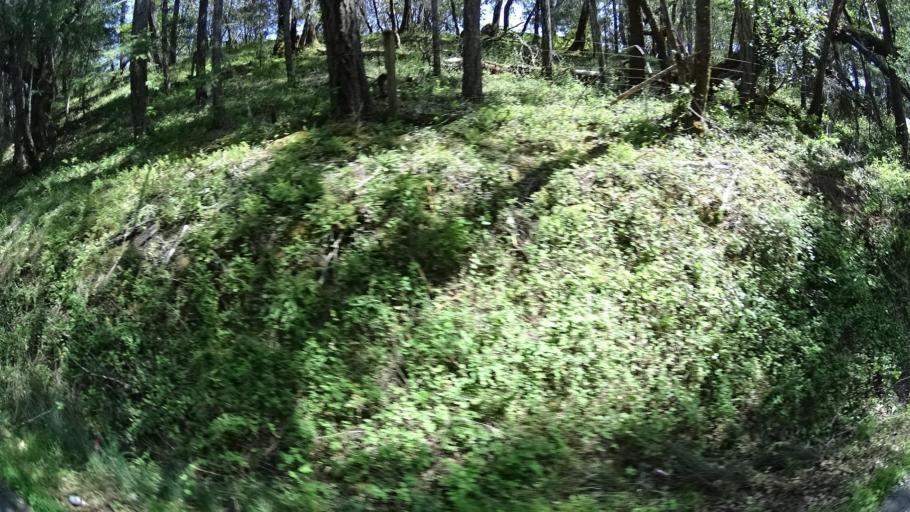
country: US
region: California
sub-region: Humboldt County
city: Redway
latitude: 40.2468
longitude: -123.6246
